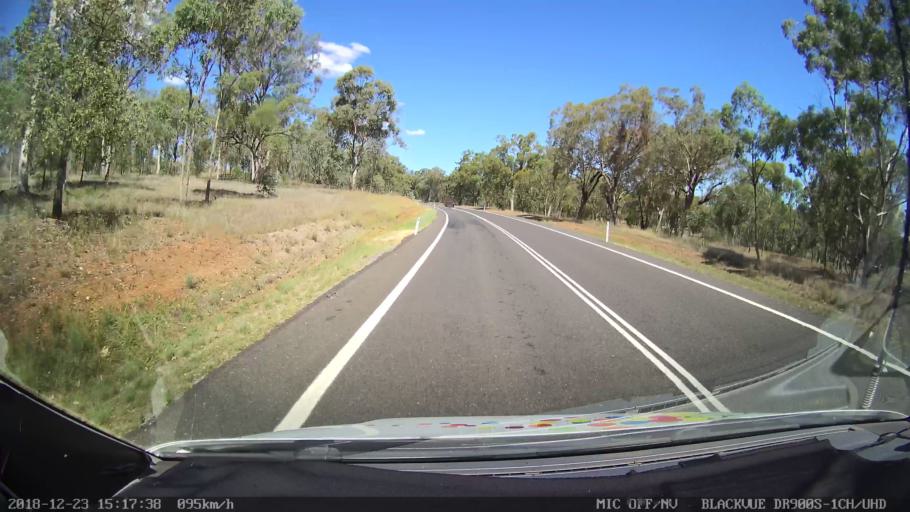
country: AU
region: New South Wales
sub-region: Tamworth Municipality
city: Manilla
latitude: -30.8106
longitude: 150.7616
